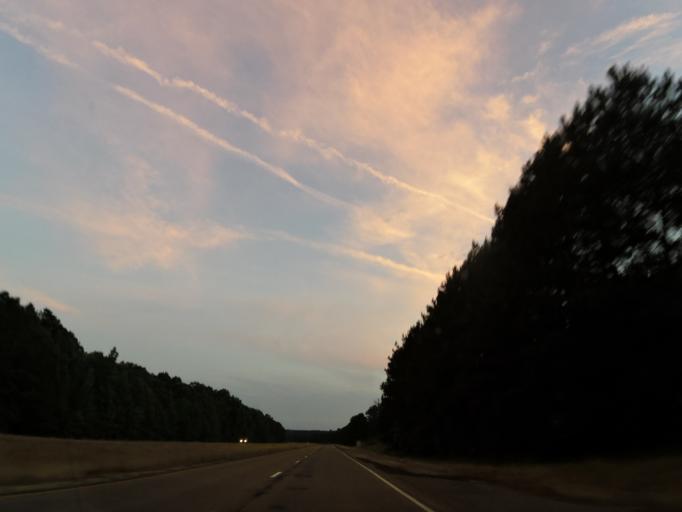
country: US
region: Mississippi
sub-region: Lauderdale County
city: Meridian Station
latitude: 32.5994
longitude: -88.4993
